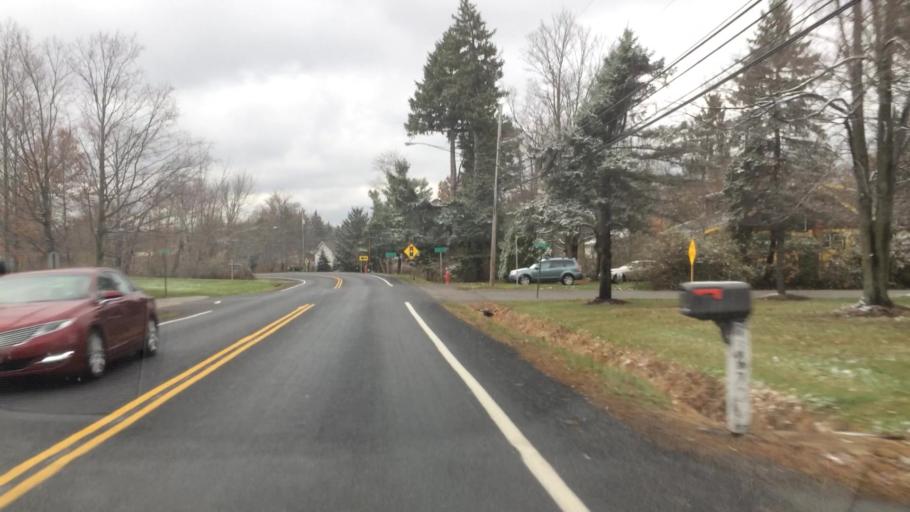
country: US
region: Ohio
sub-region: Summit County
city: Macedonia
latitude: 41.2913
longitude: -81.5197
